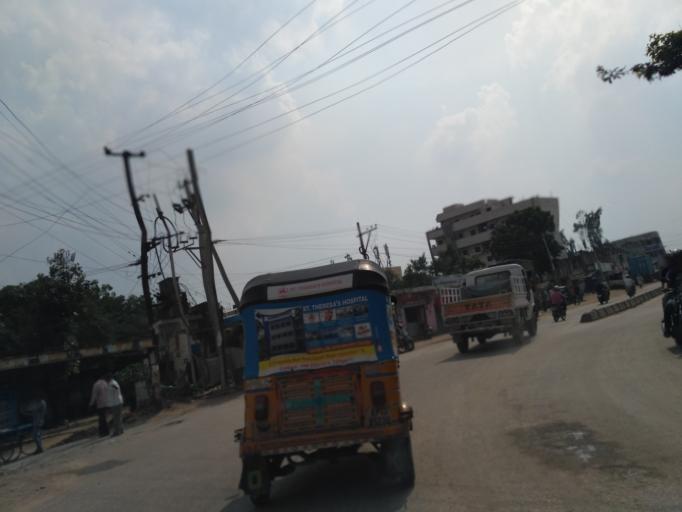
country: IN
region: Telangana
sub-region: Rangareddi
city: Kukatpalli
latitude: 17.4666
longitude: 78.4255
